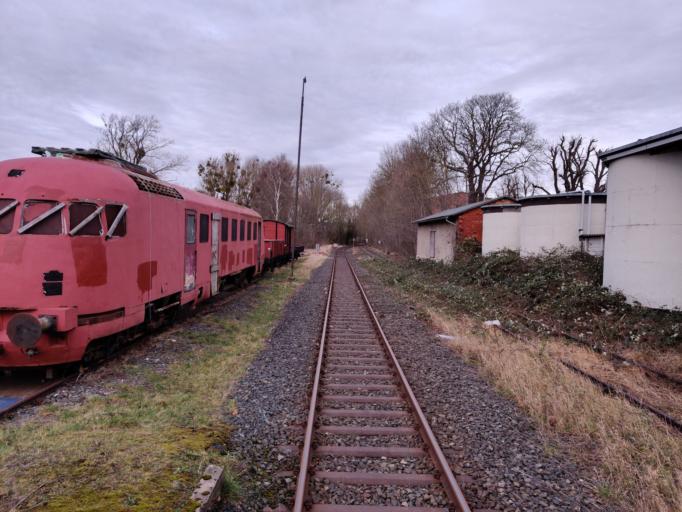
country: DE
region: Lower Saxony
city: Bockenem
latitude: 52.0122
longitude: 10.1234
